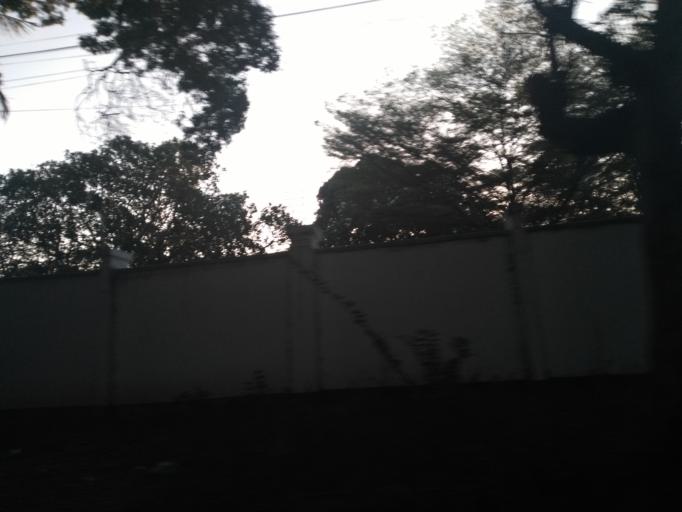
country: TZ
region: Dar es Salaam
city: Magomeni
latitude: -6.7694
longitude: 39.2783
